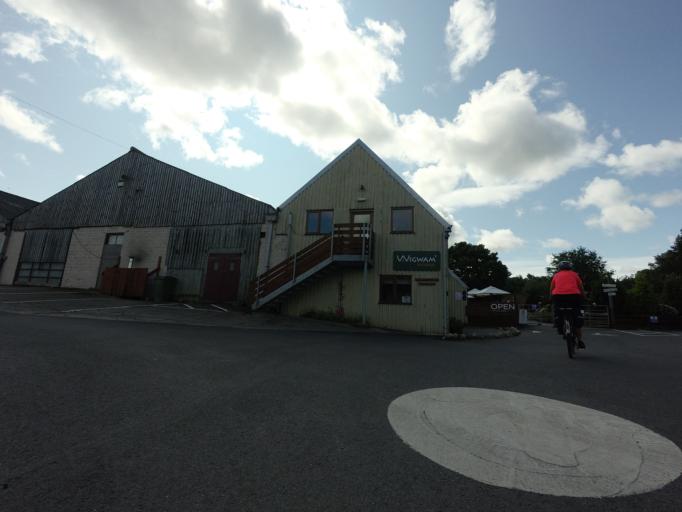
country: GB
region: Scotland
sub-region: Moray
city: Kinloss
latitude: 57.6363
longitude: -3.5181
